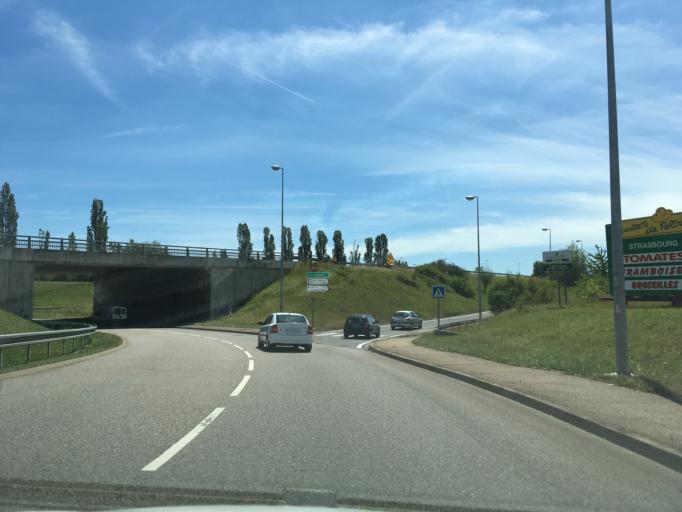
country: FR
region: Lorraine
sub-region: Departement de la Moselle
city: Peltre
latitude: 49.1069
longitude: 6.2350
